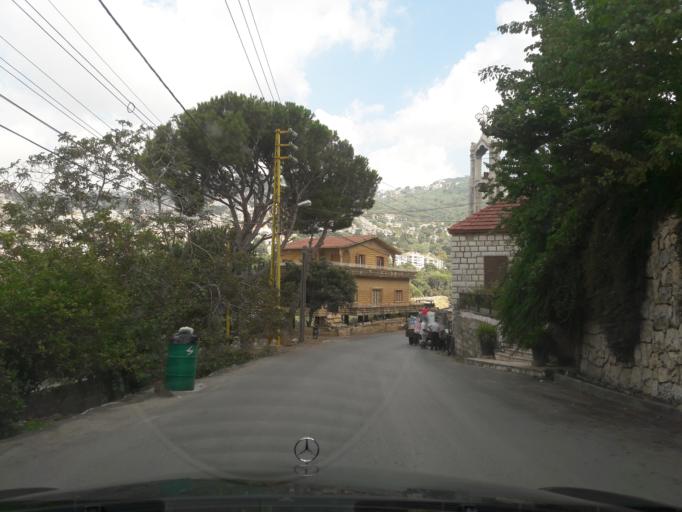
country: LB
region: Mont-Liban
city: Djounie
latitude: 33.9288
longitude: 35.6623
